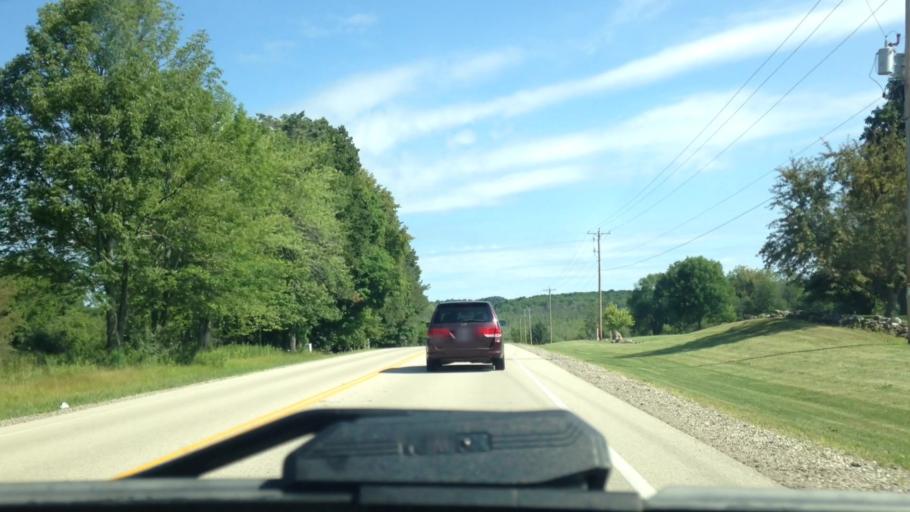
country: US
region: Wisconsin
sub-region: Washington County
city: West Bend
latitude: 43.4067
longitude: -88.2411
